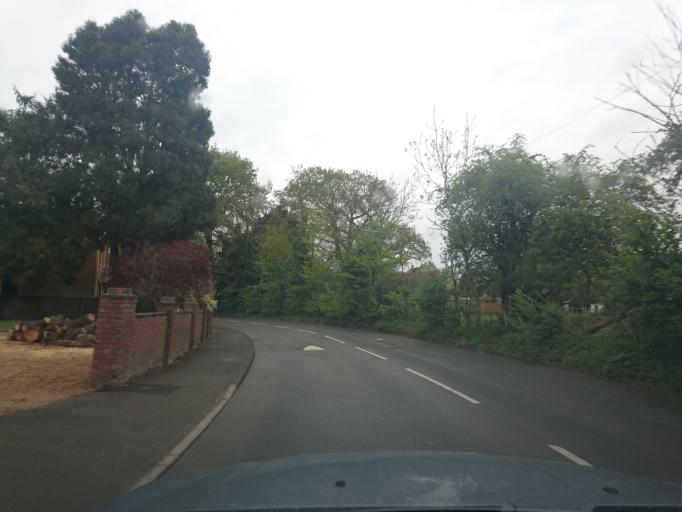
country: GB
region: England
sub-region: Surrey
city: Seale
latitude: 51.2463
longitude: -0.7146
